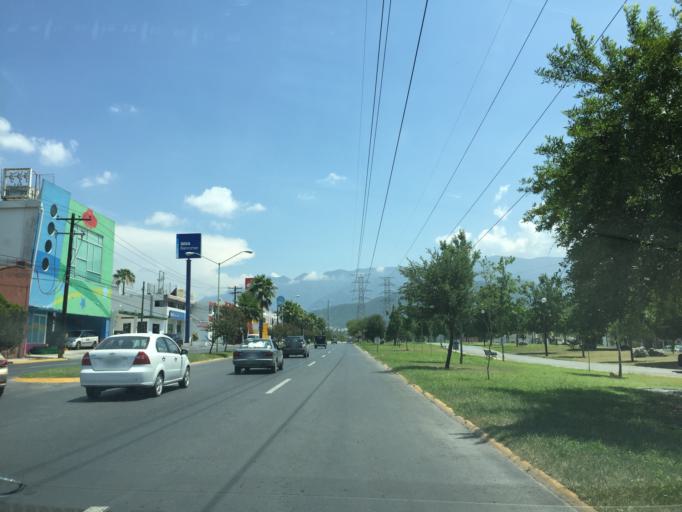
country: MX
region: Nuevo Leon
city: Guadalupe
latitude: 25.6448
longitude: -100.2683
